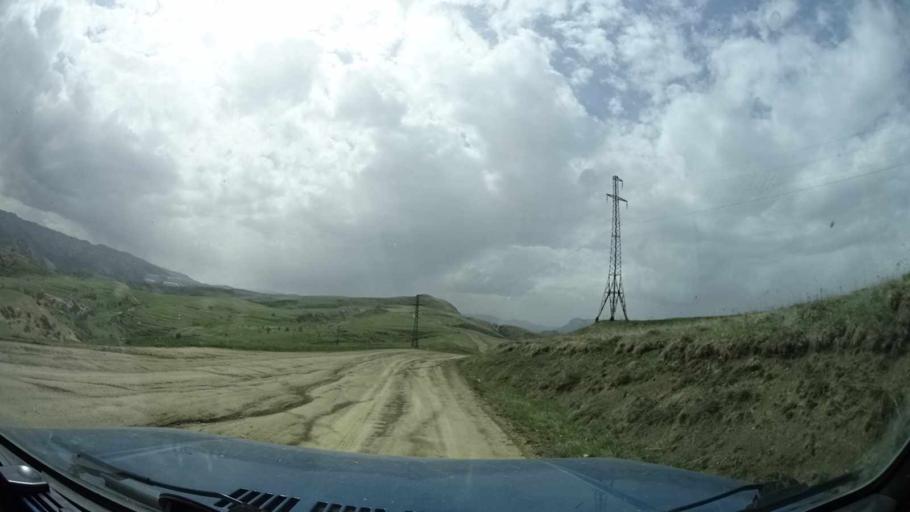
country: RU
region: Dagestan
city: Kubachi
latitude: 42.0805
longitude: 47.5569
